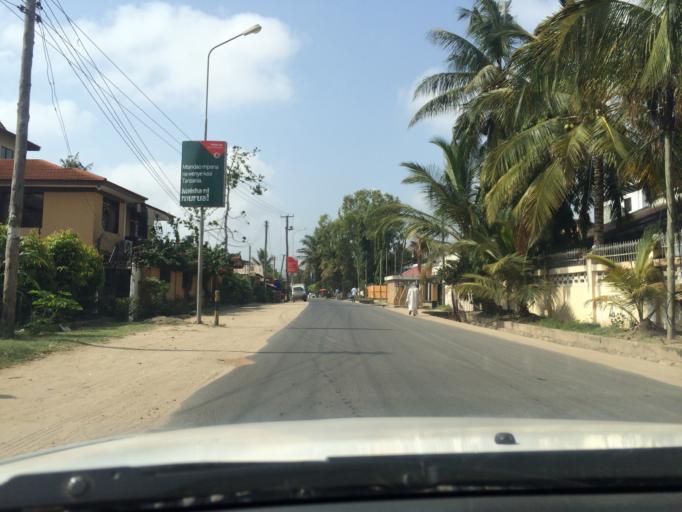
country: TZ
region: Dar es Salaam
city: Magomeni
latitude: -6.7599
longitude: 39.2714
